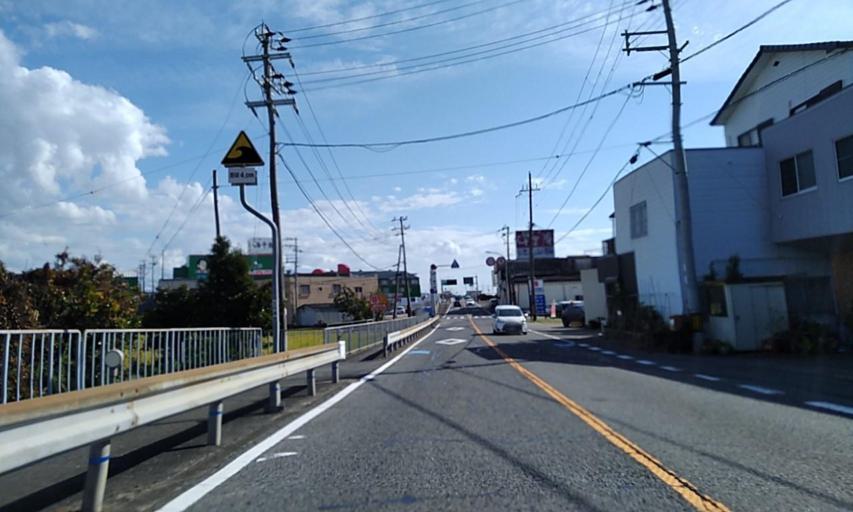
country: JP
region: Wakayama
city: Tanabe
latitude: 33.7738
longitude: 135.3127
